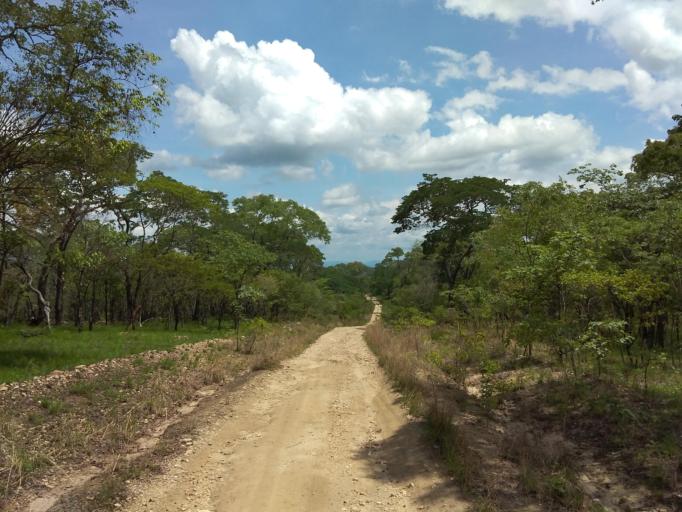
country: ZM
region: Central
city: Mkushi
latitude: -14.0752
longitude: 29.9654
